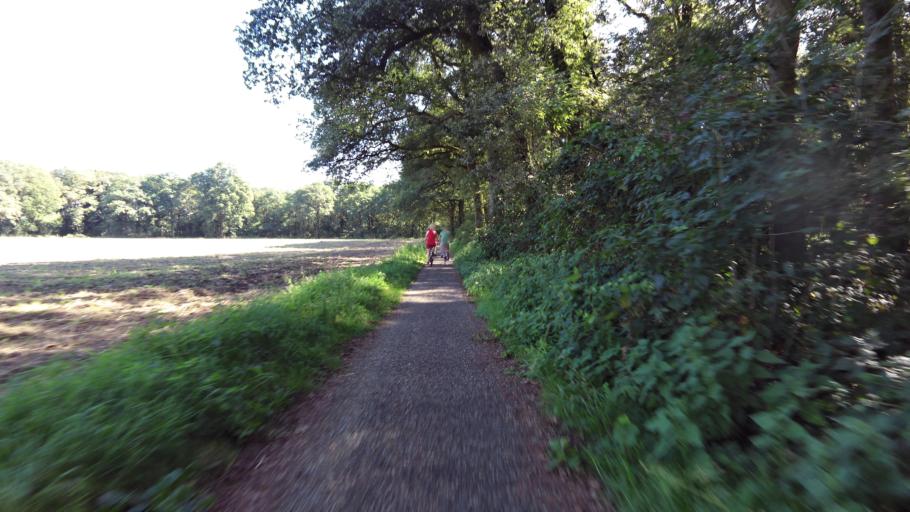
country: NL
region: Gelderland
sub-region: Gemeente Renkum
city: Doorwerth
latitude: 51.9725
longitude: 5.7777
